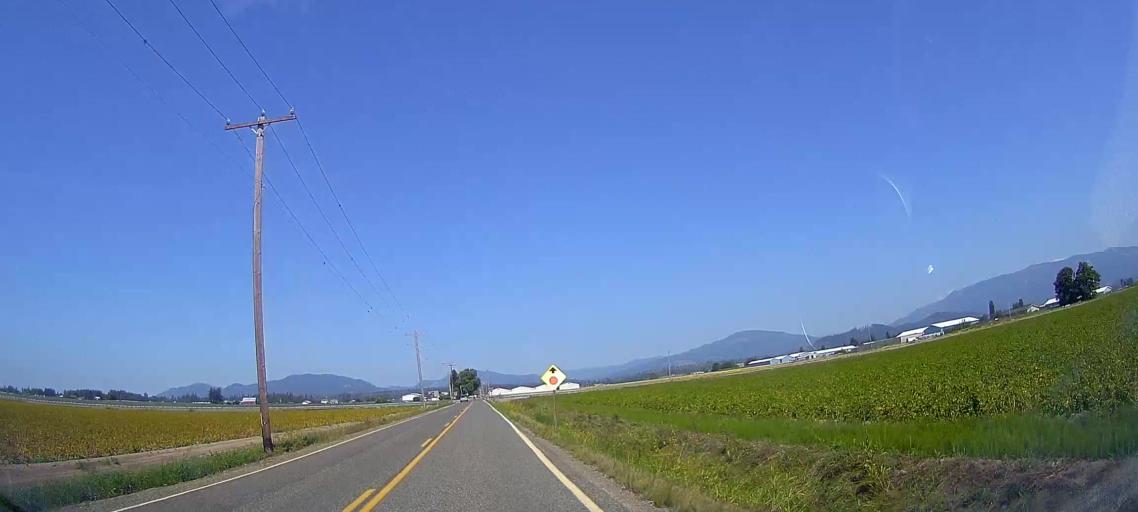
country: US
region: Washington
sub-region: Skagit County
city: Burlington
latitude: 48.4846
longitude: -122.3569
